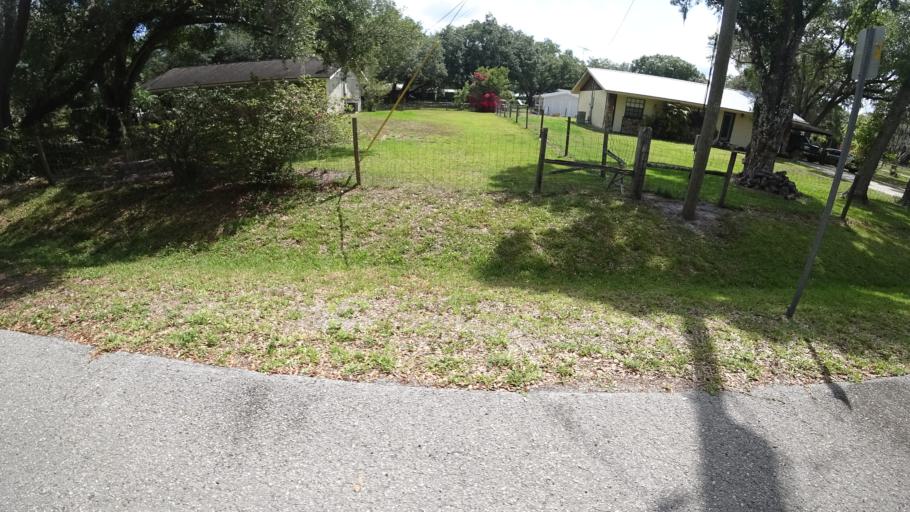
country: US
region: Florida
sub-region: Sarasota County
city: Lake Sarasota
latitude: 27.3533
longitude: -82.1646
